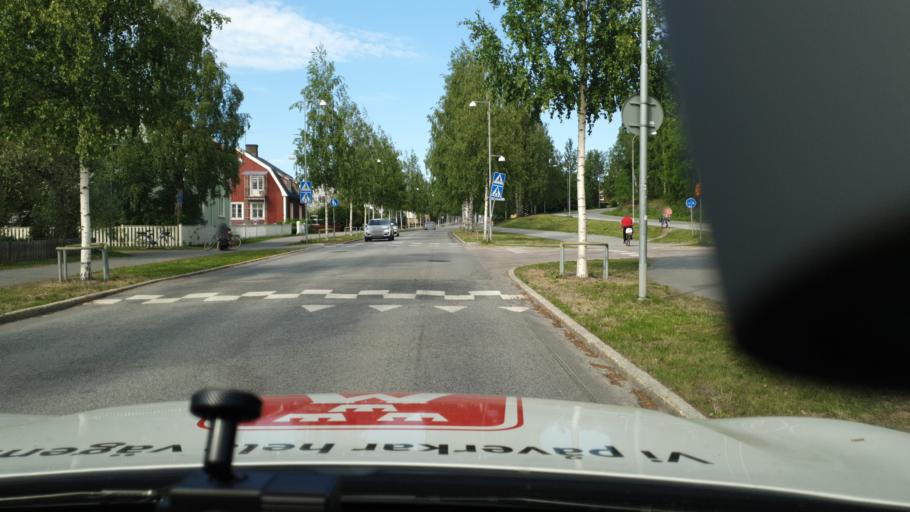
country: SE
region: Vaesterbotten
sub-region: Umea Kommun
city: Umea
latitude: 63.8408
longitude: 20.2859
